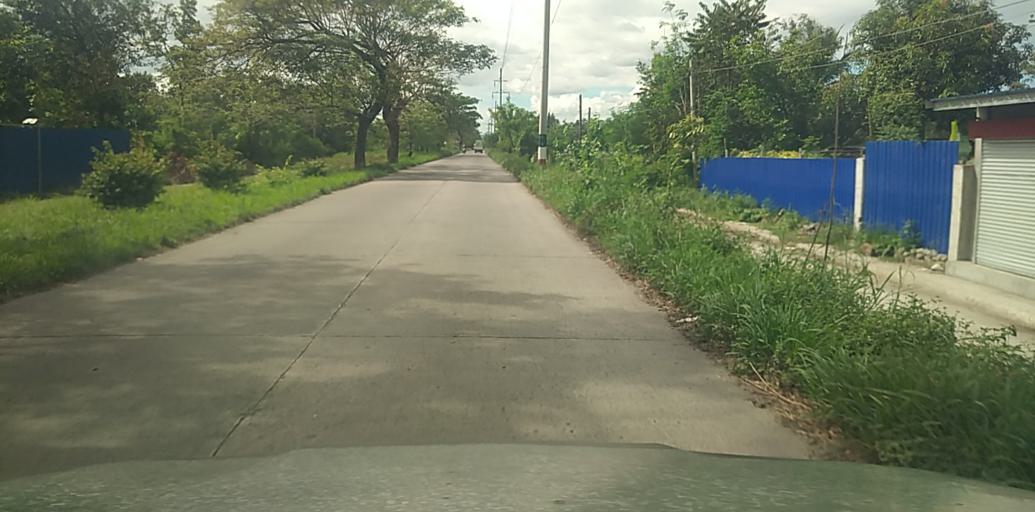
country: PH
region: Central Luzon
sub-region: Province of Pampanga
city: Pandacaqui
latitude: 15.1769
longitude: 120.6658
